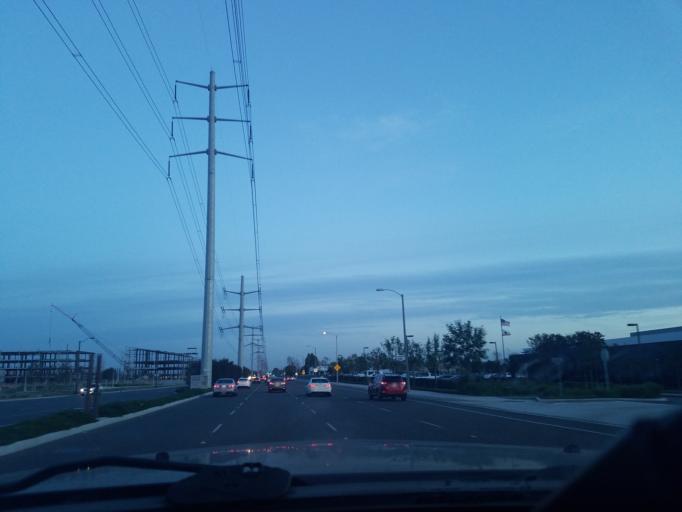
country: US
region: California
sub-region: Orange County
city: Irvine
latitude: 33.7052
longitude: -117.8428
